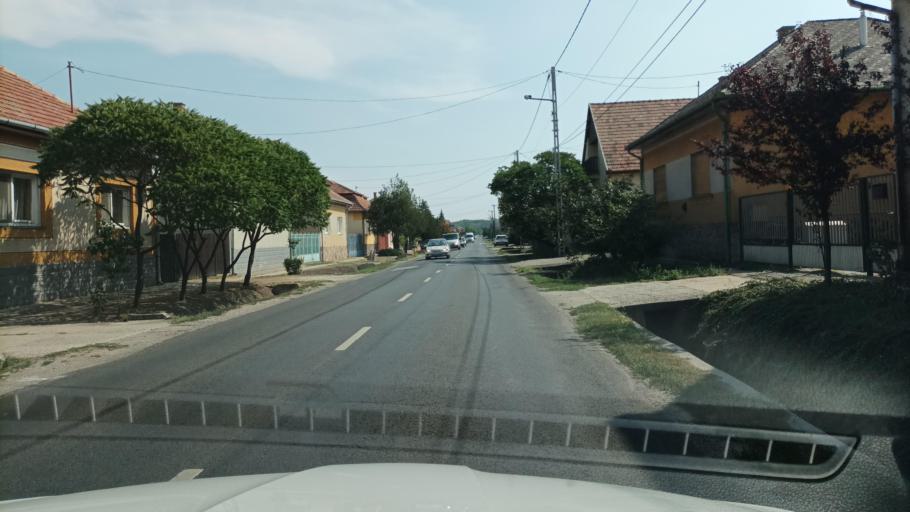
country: HU
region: Pest
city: Hevizgyoerk
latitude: 47.6268
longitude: 19.5251
